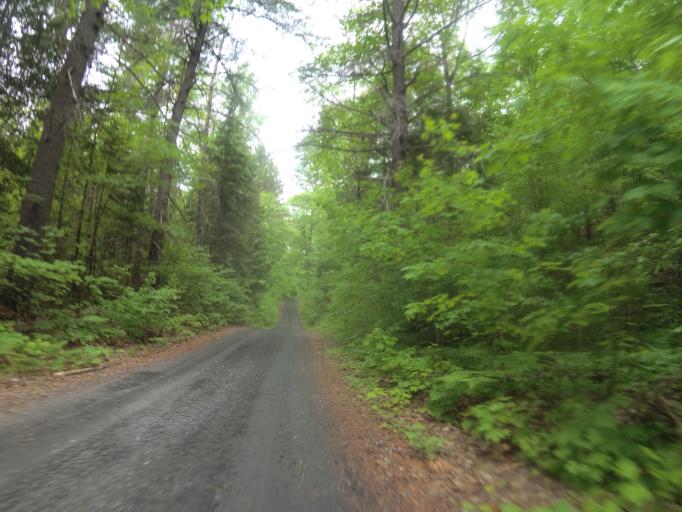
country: CA
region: Ontario
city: Renfrew
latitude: 45.1021
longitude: -76.8296
